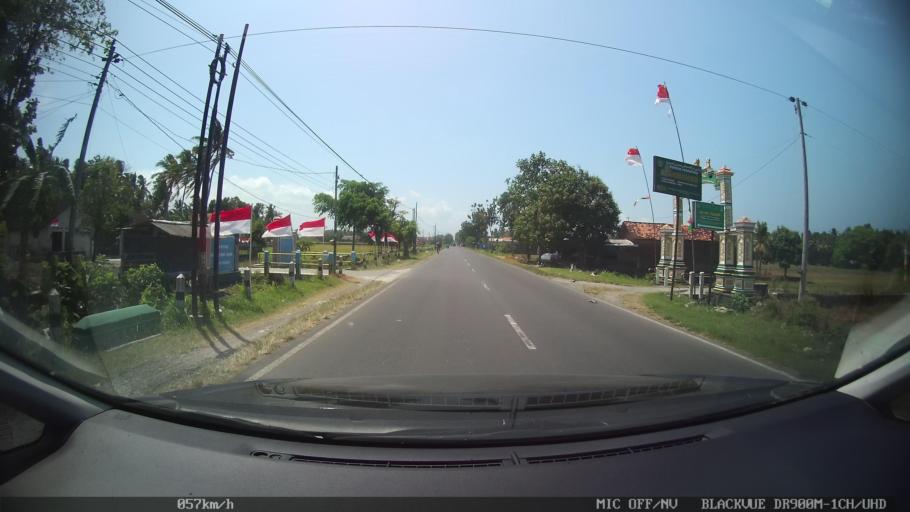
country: ID
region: Daerah Istimewa Yogyakarta
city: Srandakan
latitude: -7.9523
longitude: 110.2000
